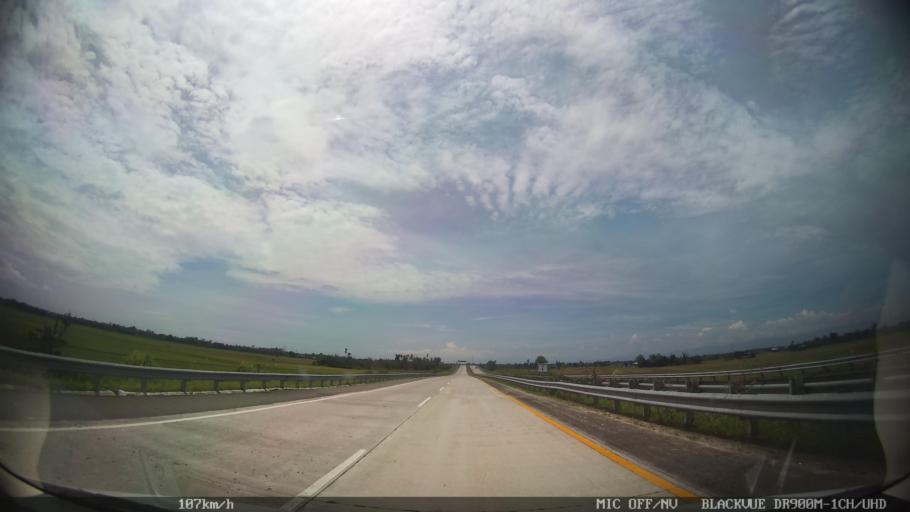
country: ID
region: North Sumatra
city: Percut
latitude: 3.5782
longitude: 98.8471
